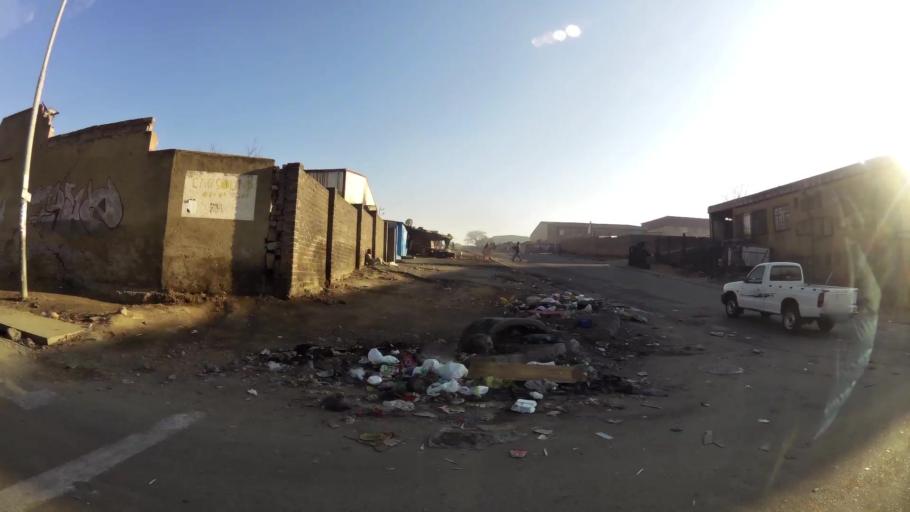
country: ZA
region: Gauteng
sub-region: City of Johannesburg Metropolitan Municipality
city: Modderfontein
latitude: -26.0987
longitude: 28.0939
